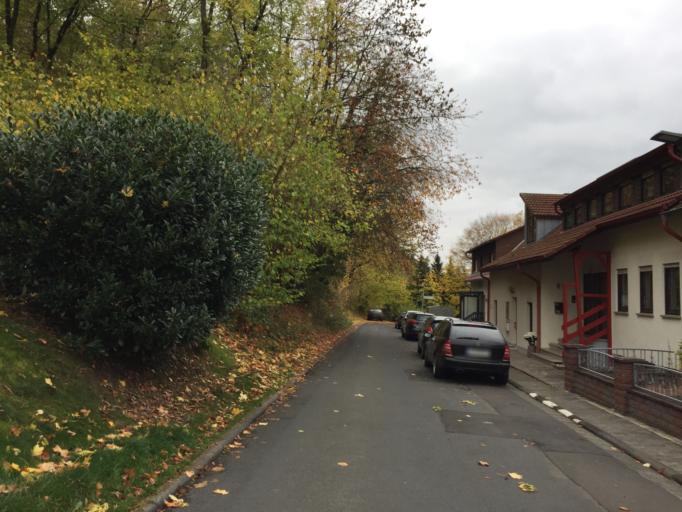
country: DE
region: Hesse
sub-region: Regierungsbezirk Giessen
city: Lich
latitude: 50.5144
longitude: 8.8119
